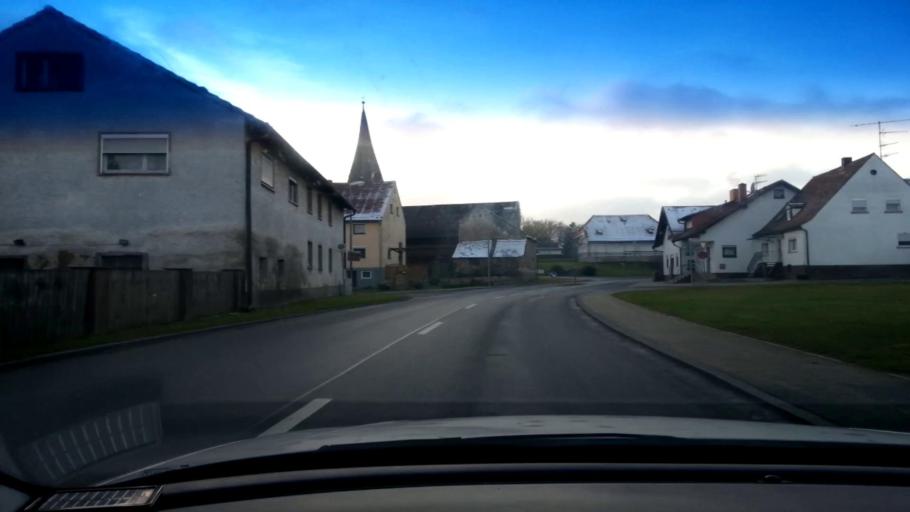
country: DE
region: Bavaria
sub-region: Upper Franconia
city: Frensdorf
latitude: 49.7933
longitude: 10.8879
